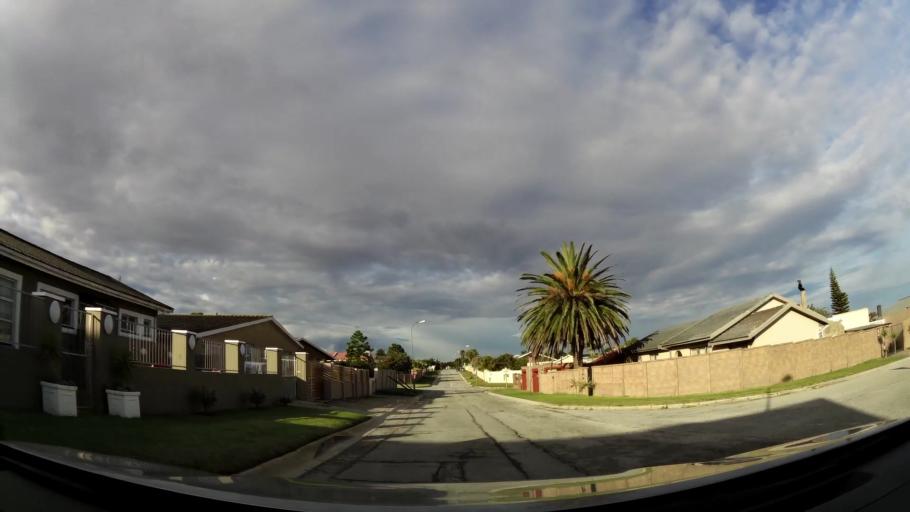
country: ZA
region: Eastern Cape
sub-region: Nelson Mandela Bay Metropolitan Municipality
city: Port Elizabeth
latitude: -33.9463
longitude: 25.4849
